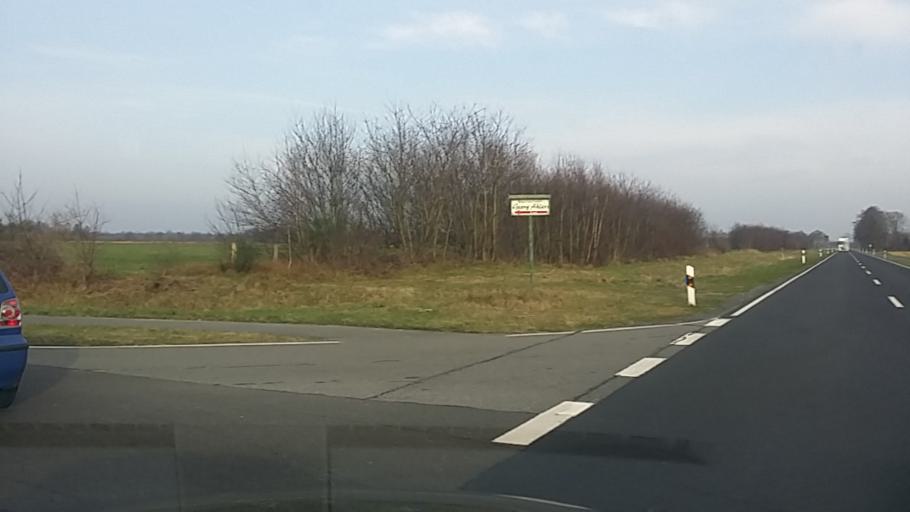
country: DE
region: Lower Saxony
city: Geeste
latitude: 52.5965
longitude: 7.1855
